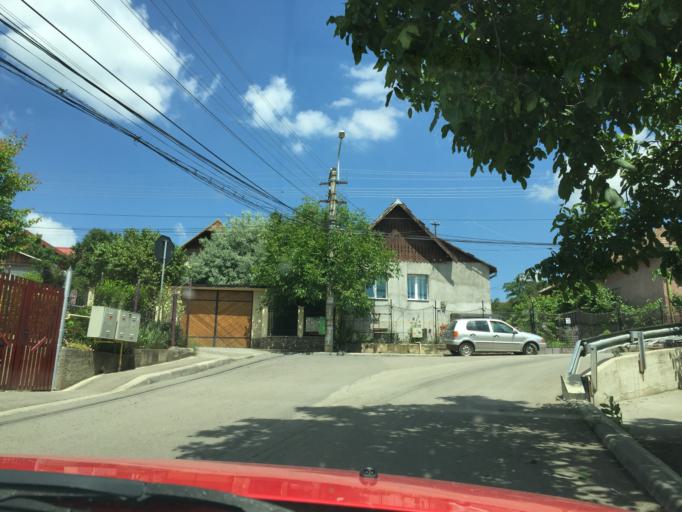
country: RO
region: Cluj
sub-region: Municipiul Cluj-Napoca
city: Cluj-Napoca
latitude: 46.7937
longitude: 23.5785
